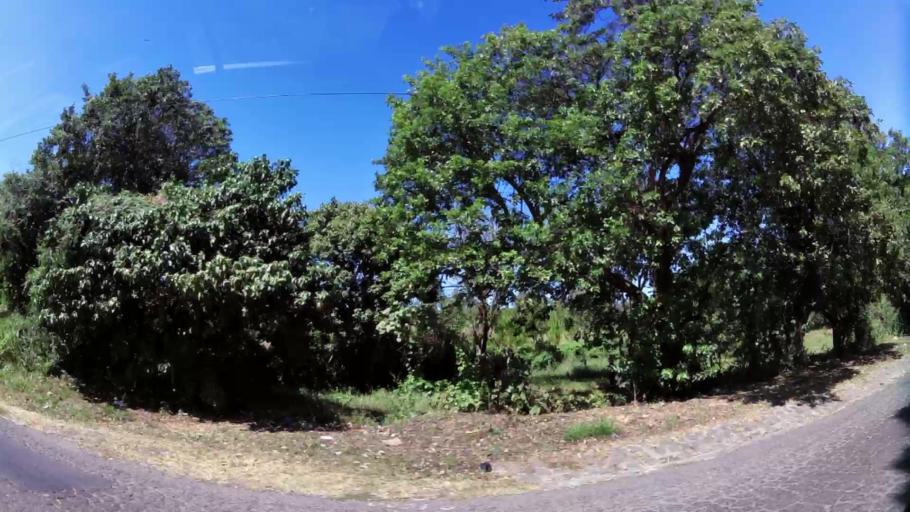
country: SV
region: Ahuachapan
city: Ahuachapan
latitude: 13.9466
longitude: -89.8194
